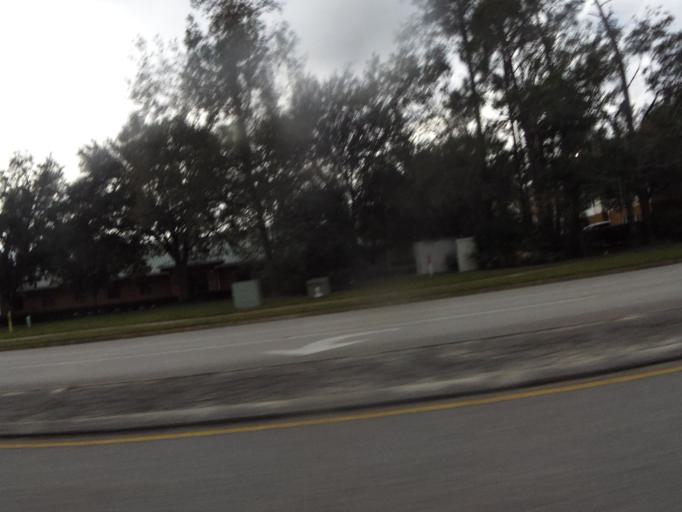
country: US
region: Florida
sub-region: Duval County
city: Jacksonville
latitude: 30.2462
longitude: -81.5833
